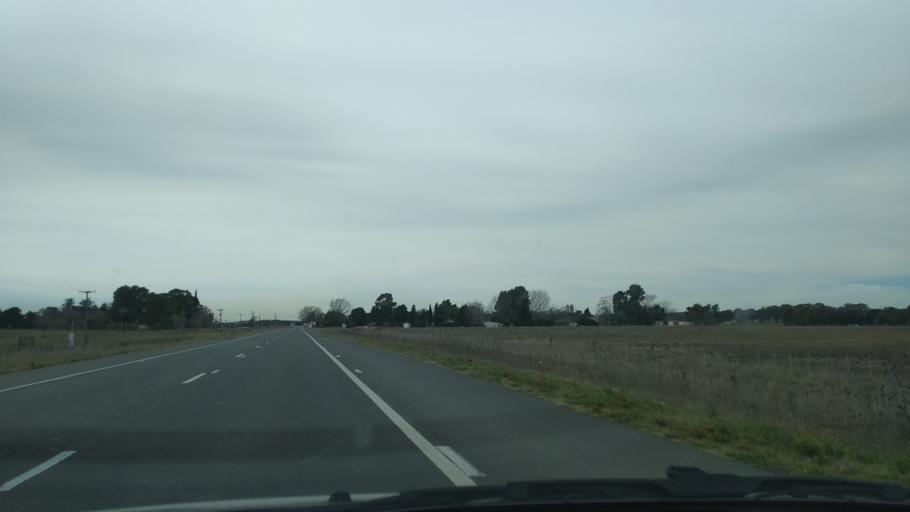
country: AR
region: Buenos Aires
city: Olavarria
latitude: -36.9911
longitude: -60.3164
